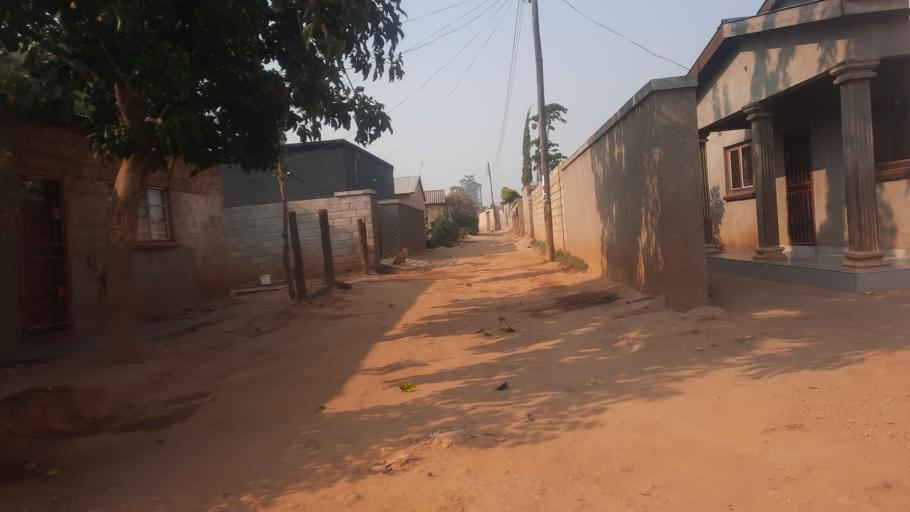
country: ZM
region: Lusaka
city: Lusaka
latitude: -15.3957
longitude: 28.3837
